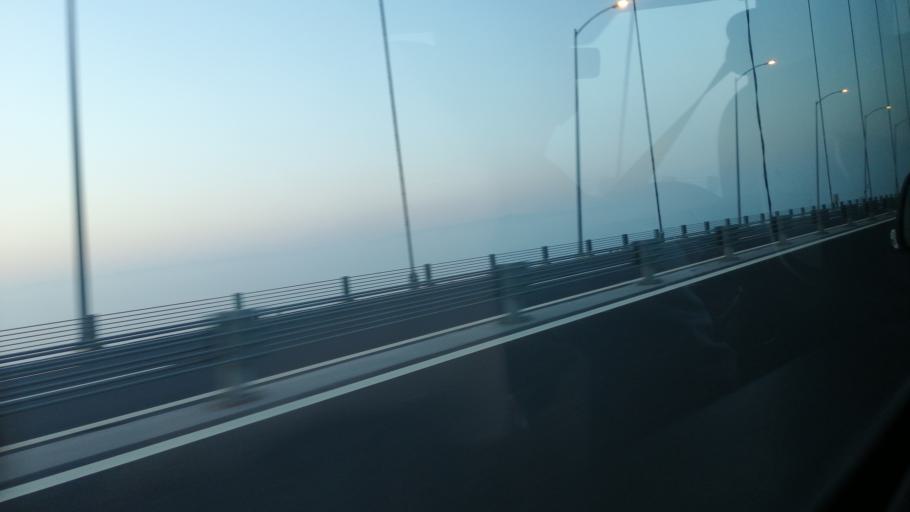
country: TR
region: Kocaeli
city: Tavsancil
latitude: 40.7595
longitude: 29.5167
